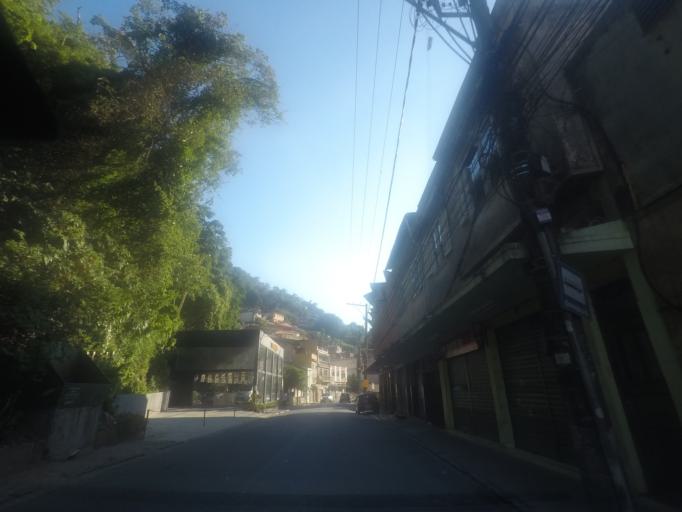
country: BR
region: Rio de Janeiro
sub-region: Petropolis
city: Petropolis
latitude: -22.4938
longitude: -43.1585
